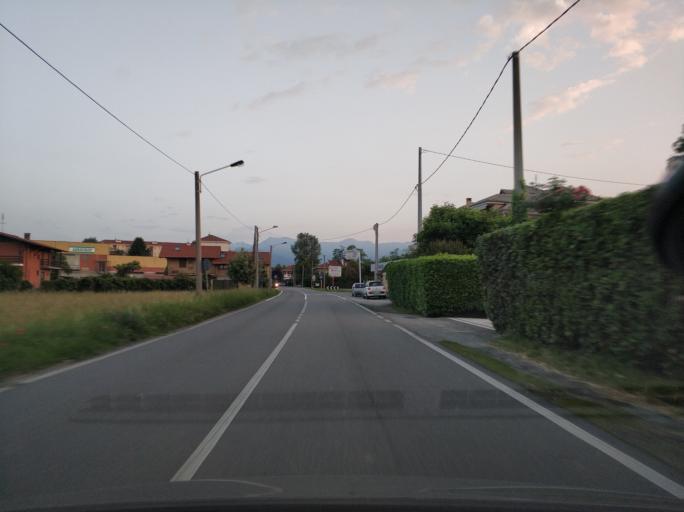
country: IT
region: Piedmont
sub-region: Provincia di Torino
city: Cirie
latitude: 45.2293
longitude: 7.6166
